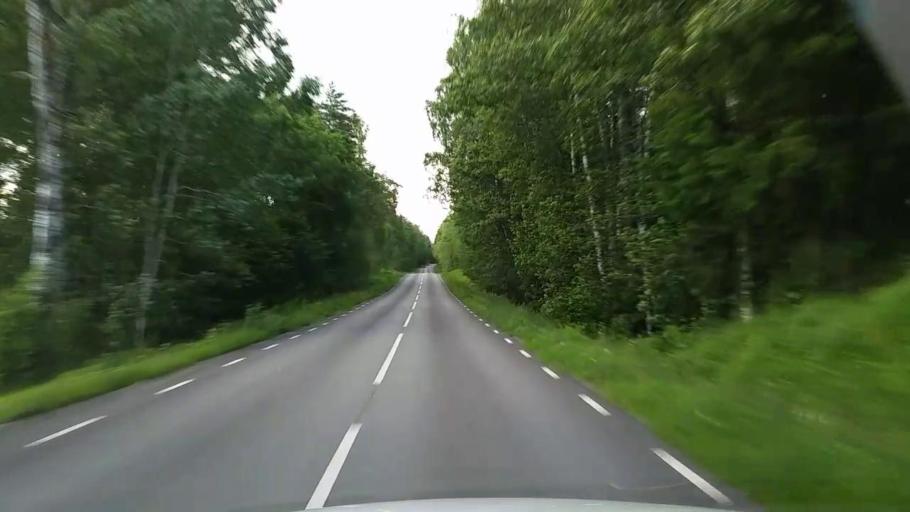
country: SE
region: Vaestmanland
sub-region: Kopings Kommun
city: Kolsva
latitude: 59.7473
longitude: 15.8300
